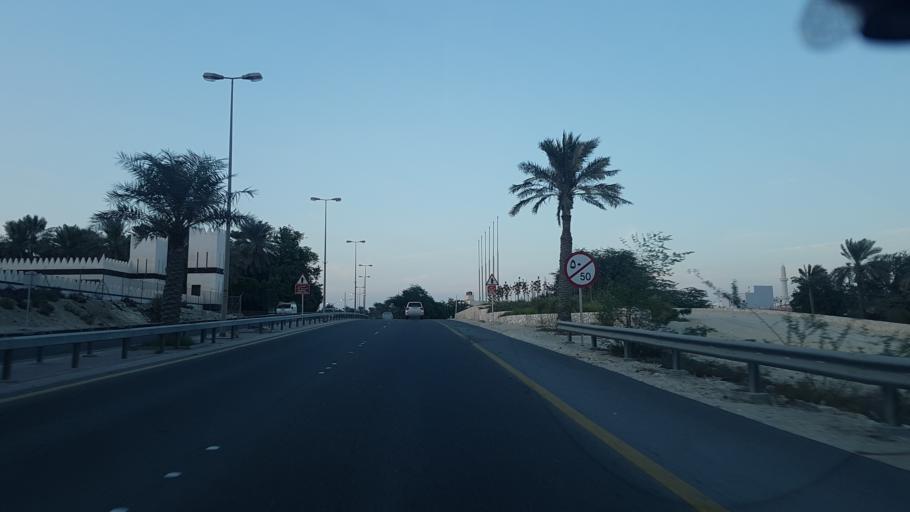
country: BH
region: Northern
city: Ar Rifa'
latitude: 26.1177
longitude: 50.5371
